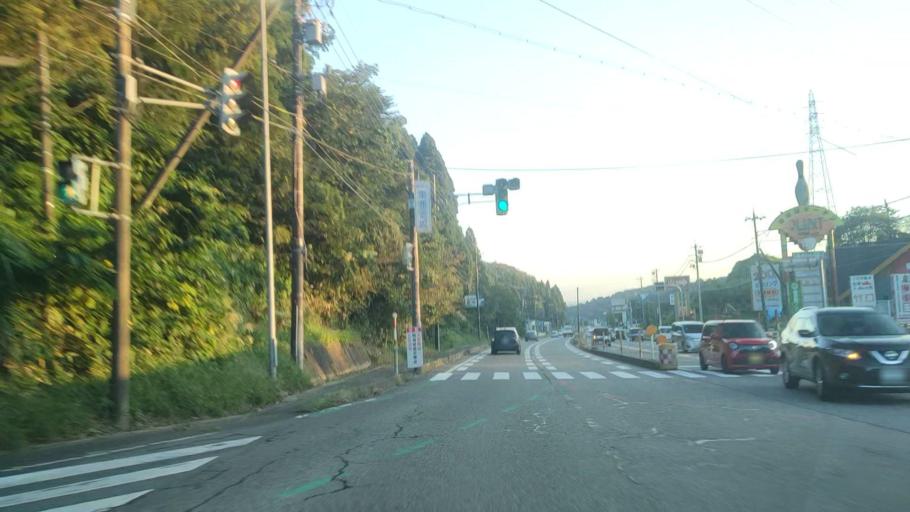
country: JP
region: Toyama
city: Takaoka
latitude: 36.7937
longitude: 137.0020
